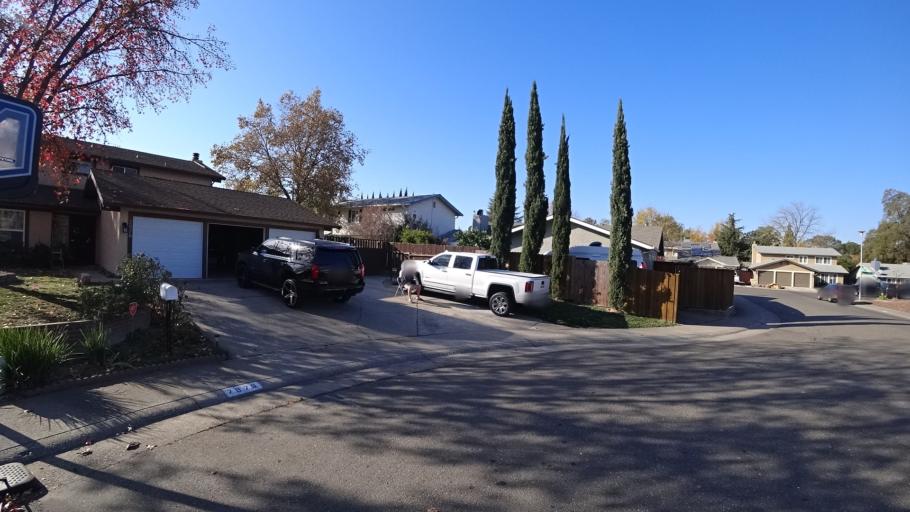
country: US
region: California
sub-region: Sacramento County
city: Citrus Heights
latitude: 38.6971
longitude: -121.2730
